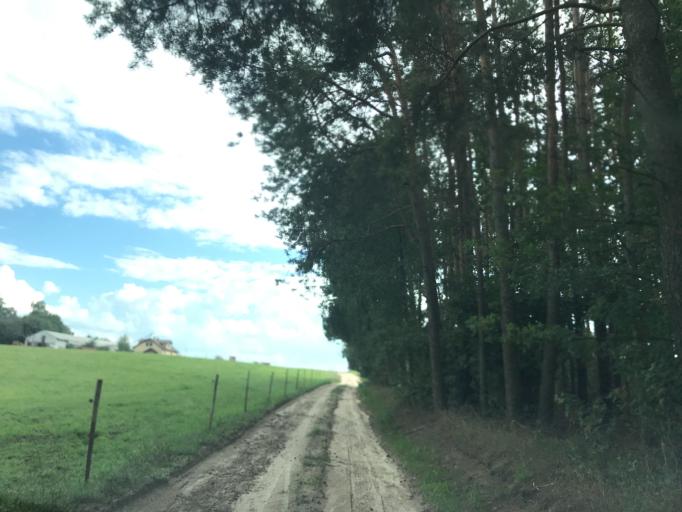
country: PL
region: Kujawsko-Pomorskie
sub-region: Powiat brodnicki
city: Brzozie
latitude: 53.3233
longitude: 19.6884
